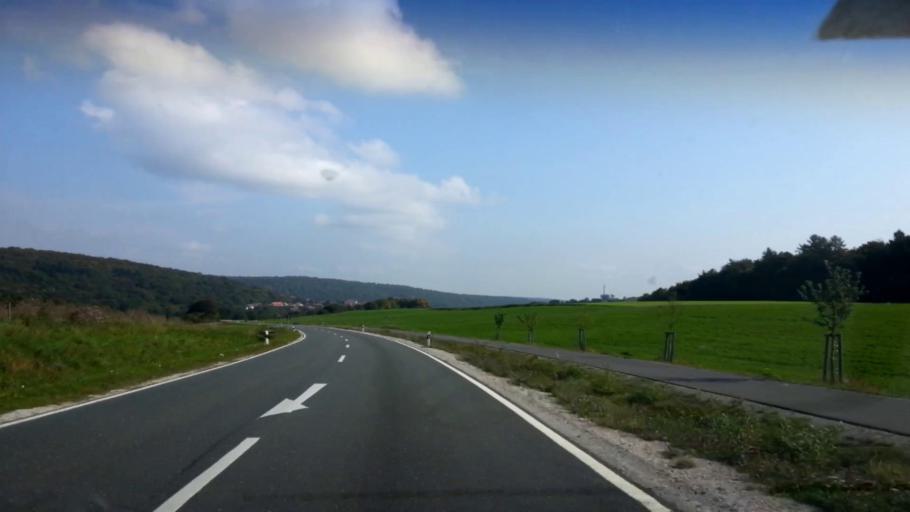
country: DE
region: Bavaria
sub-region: Regierungsbezirk Unterfranken
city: Oberschwarzach
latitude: 49.8481
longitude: 10.4763
